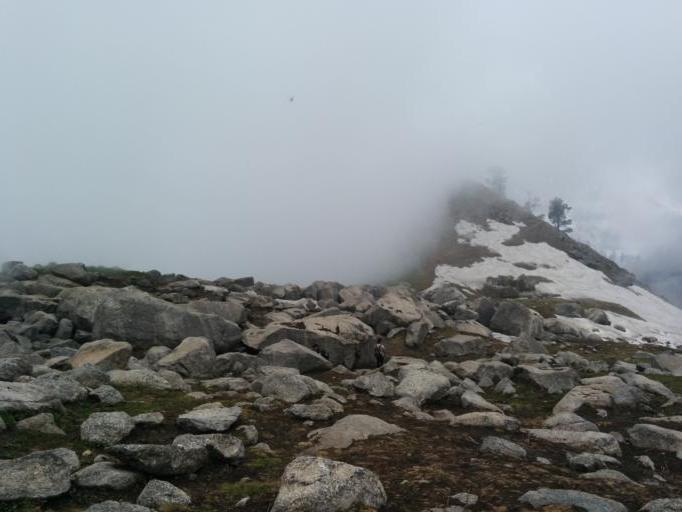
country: IN
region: Himachal Pradesh
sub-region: Kangra
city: Dharmsala
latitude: 32.2820
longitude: 76.3640
